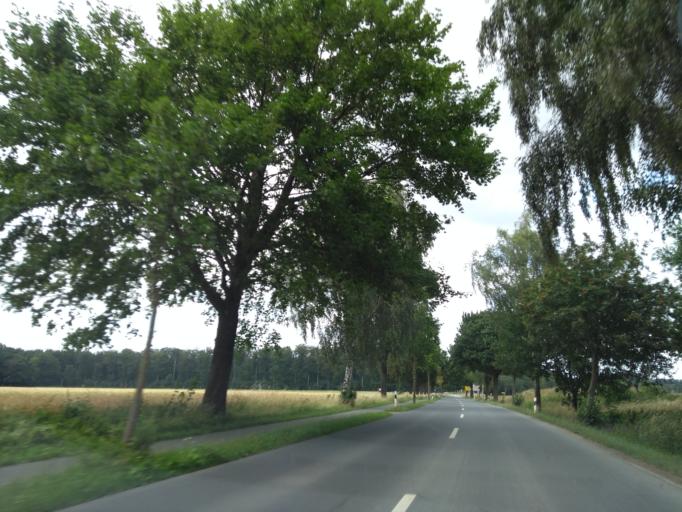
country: DE
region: North Rhine-Westphalia
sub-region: Regierungsbezirk Detmold
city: Salzkotten
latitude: 51.6556
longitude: 8.6711
